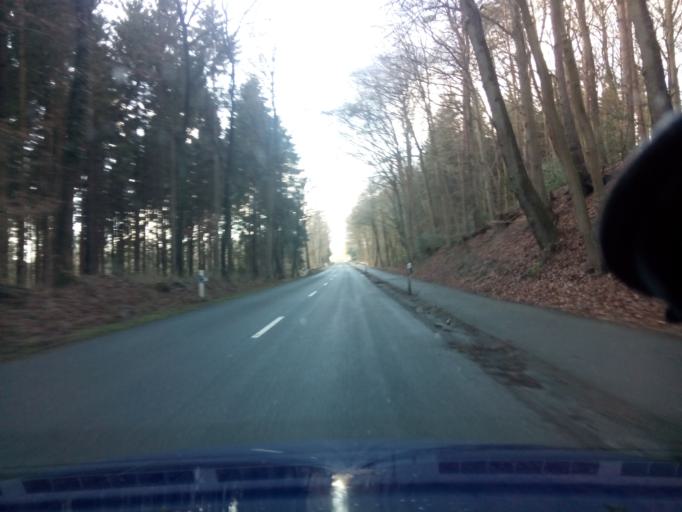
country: DE
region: Lower Saxony
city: Gnarrenburg
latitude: 53.4118
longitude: 9.0044
